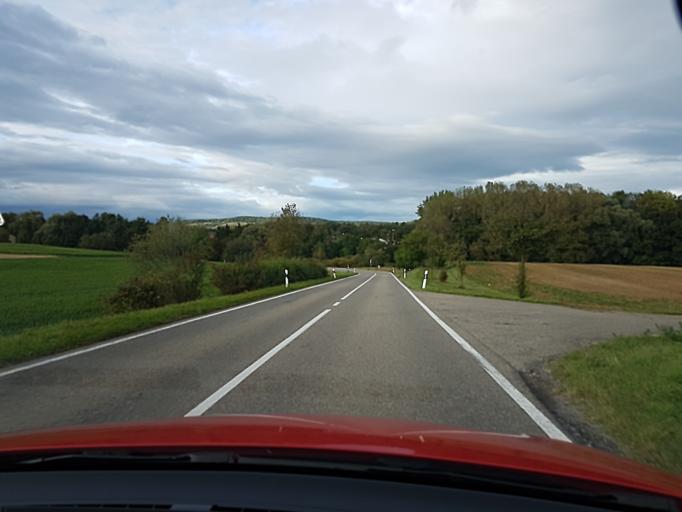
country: DE
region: Baden-Wuerttemberg
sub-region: Karlsruhe Region
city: Sternenfels
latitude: 49.0016
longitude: 8.8630
